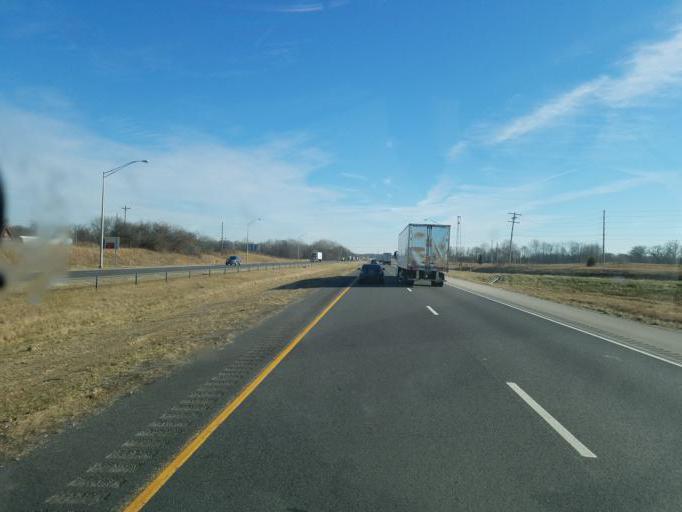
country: US
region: Indiana
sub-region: Wayne County
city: Cambridge City
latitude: 39.8529
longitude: -85.1417
